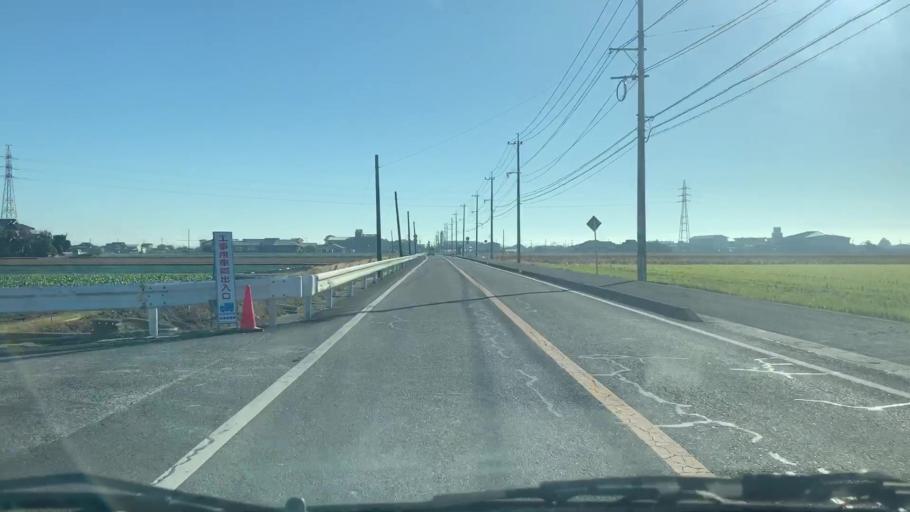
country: JP
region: Saga Prefecture
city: Kashima
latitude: 33.1920
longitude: 130.1254
